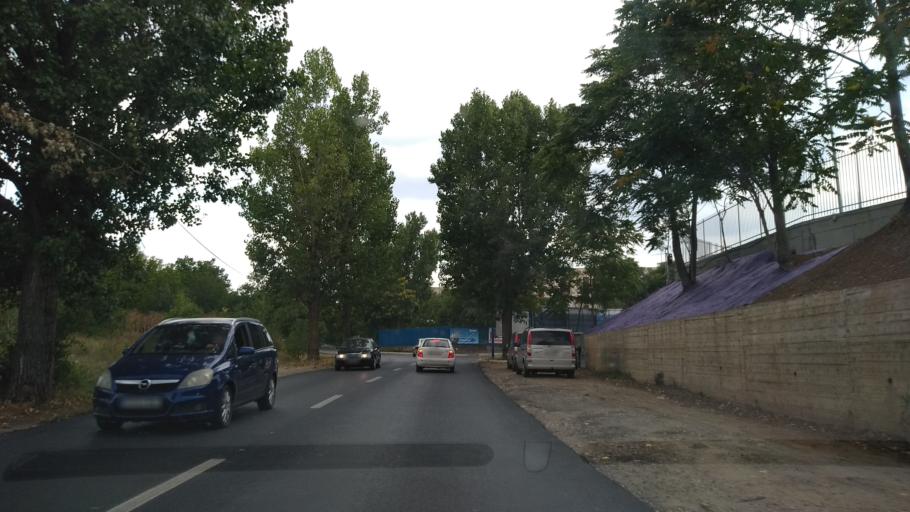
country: RO
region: Ilfov
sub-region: Comuna Popesti-Leordeni
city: Popesti-Leordeni
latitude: 44.3893
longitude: 26.1465
